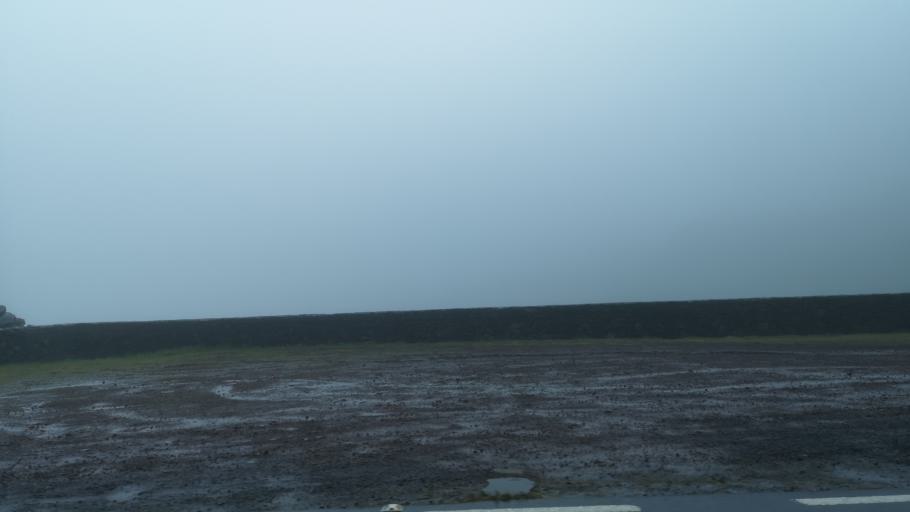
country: ES
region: Canary Islands
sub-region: Provincia de Santa Cruz de Tenerife
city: Alajero
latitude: 28.1005
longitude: -17.2030
